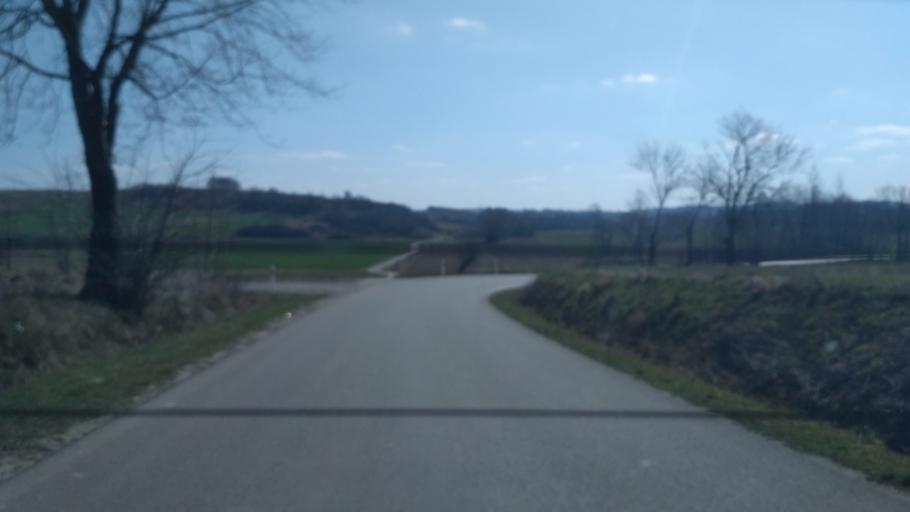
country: PL
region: Subcarpathian Voivodeship
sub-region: Powiat przeworski
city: Pantalowice
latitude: 49.9478
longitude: 22.4401
